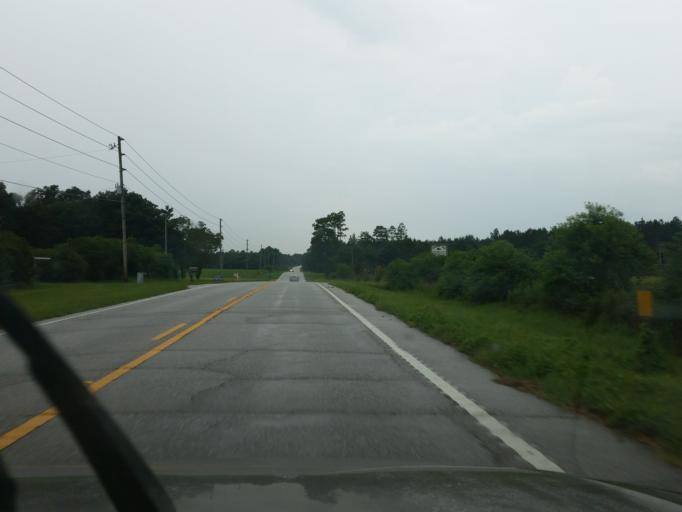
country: US
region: Alabama
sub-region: Baldwin County
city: Elberta
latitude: 30.5388
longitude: -87.5498
